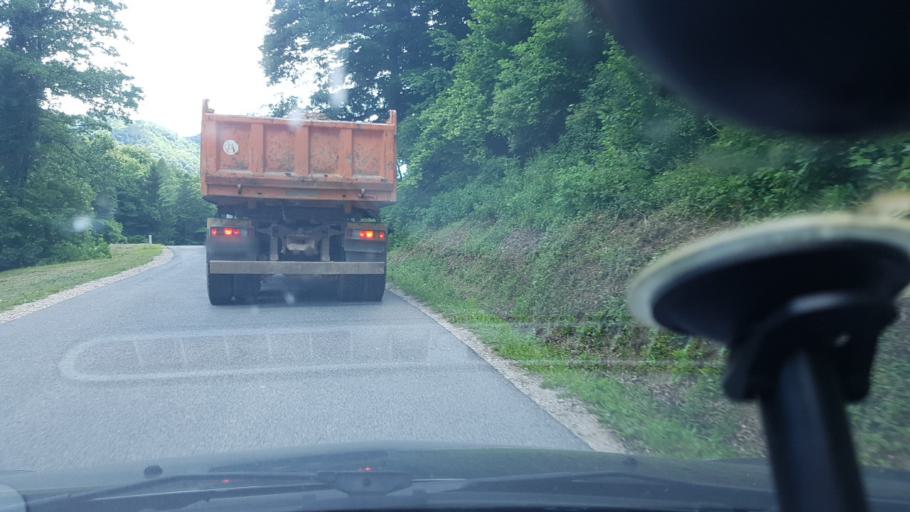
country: SI
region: Rogatec
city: Rogatec
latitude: 46.2572
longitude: 15.7560
